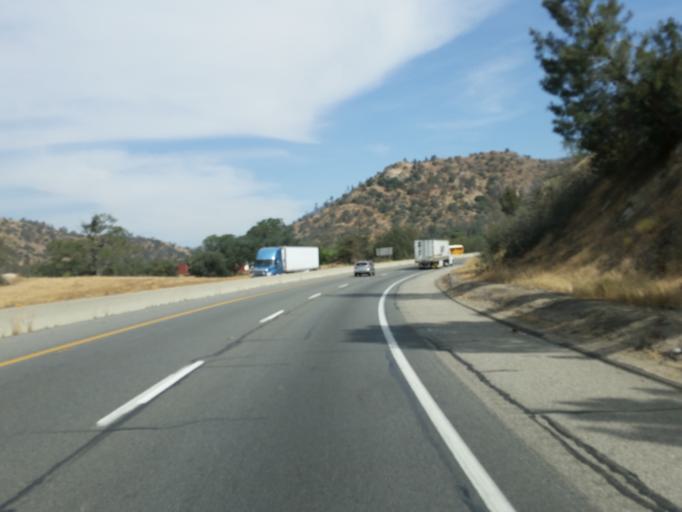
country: US
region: California
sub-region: Kern County
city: Bear Valley Springs
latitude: 35.2301
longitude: -118.5693
